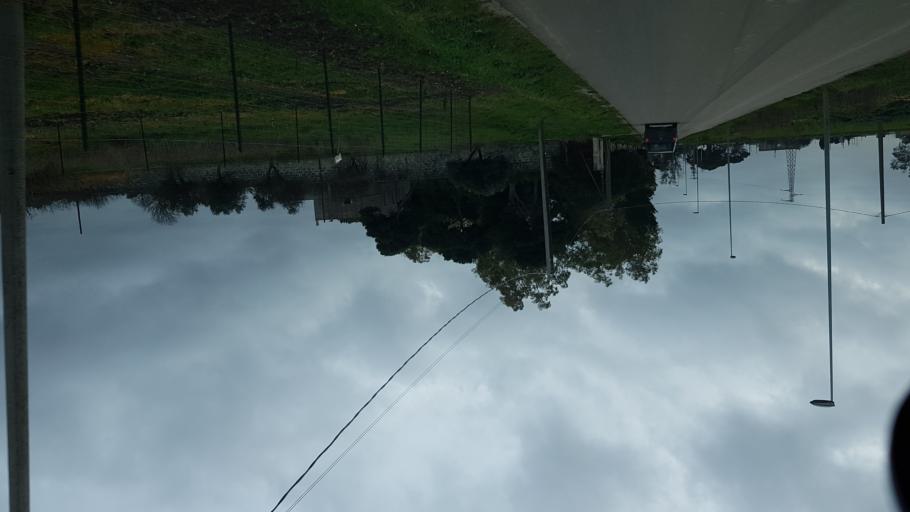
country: IT
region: Apulia
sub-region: Provincia di Brindisi
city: Brindisi
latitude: 40.6376
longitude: 17.8676
